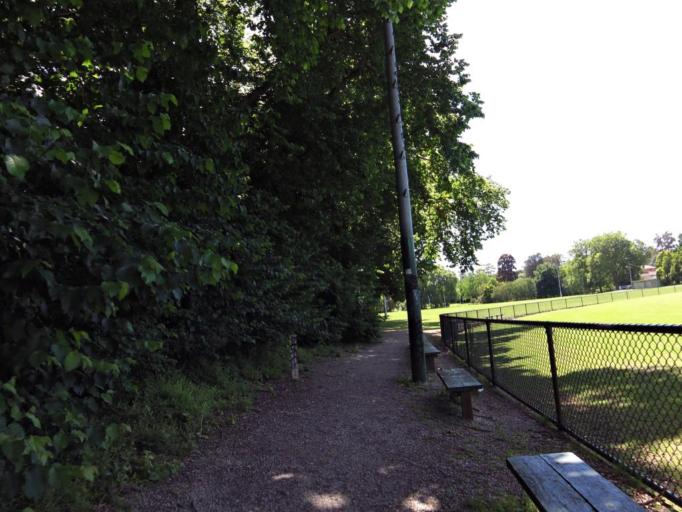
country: AU
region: Victoria
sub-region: Yarra Ranges
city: Lilydale
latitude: -37.7552
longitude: 145.3487
